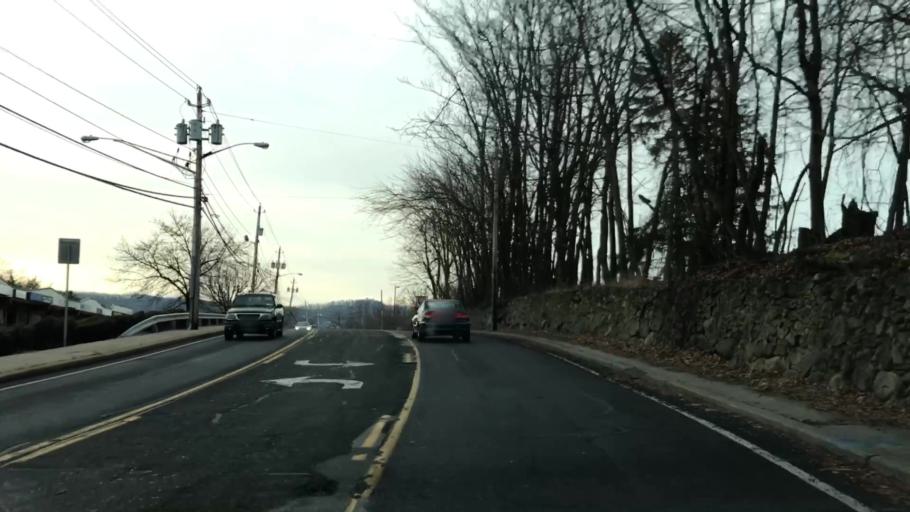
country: US
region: New York
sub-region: Rockland County
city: Stony Point
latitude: 41.2203
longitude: -73.9864
